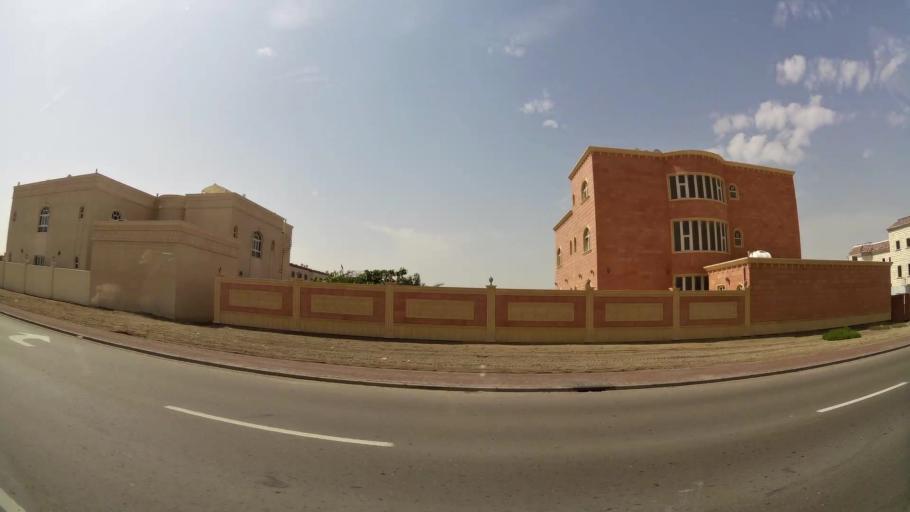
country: AE
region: Abu Dhabi
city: Abu Dhabi
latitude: 24.3219
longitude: 54.5744
